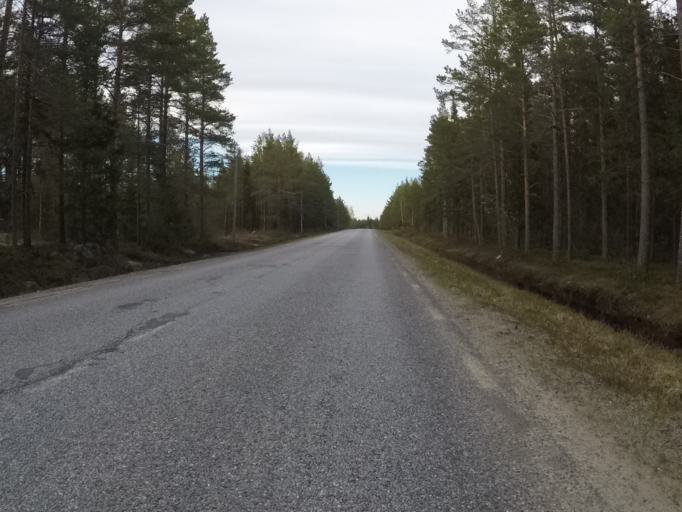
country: SE
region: Vaesterbotten
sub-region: Umea Kommun
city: Saevar
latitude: 63.9259
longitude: 20.7737
